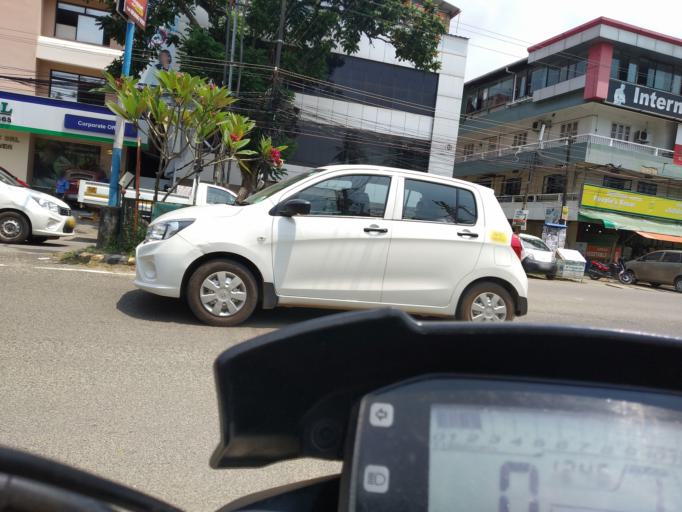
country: IN
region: Kerala
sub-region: Ernakulam
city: Cochin
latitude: 9.9639
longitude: 76.2950
